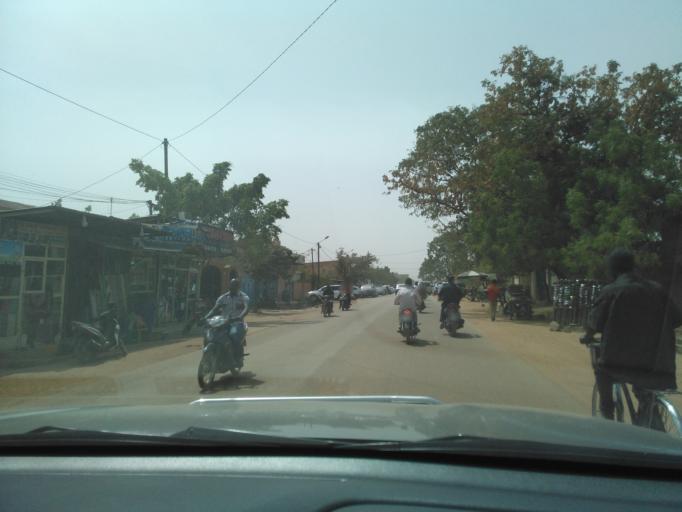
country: BF
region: Centre
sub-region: Kadiogo Province
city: Ouagadougou
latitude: 12.3555
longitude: -1.5390
